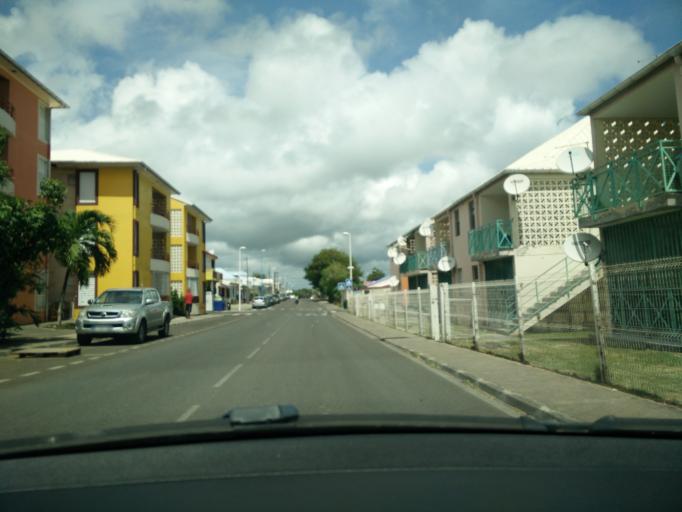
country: GP
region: Guadeloupe
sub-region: Guadeloupe
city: Le Moule
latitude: 16.3294
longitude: -61.3480
